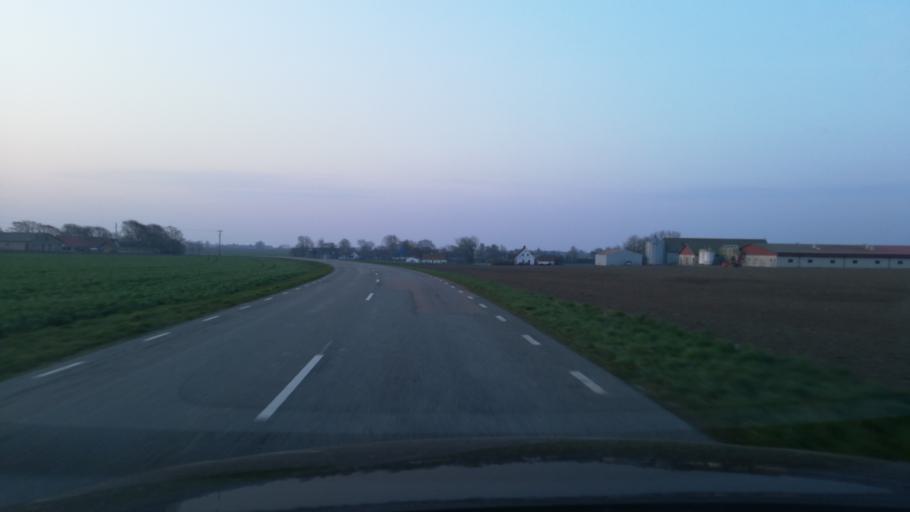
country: SE
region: Skane
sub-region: Tomelilla Kommun
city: Tomelilla
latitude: 55.4652
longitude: 14.0980
